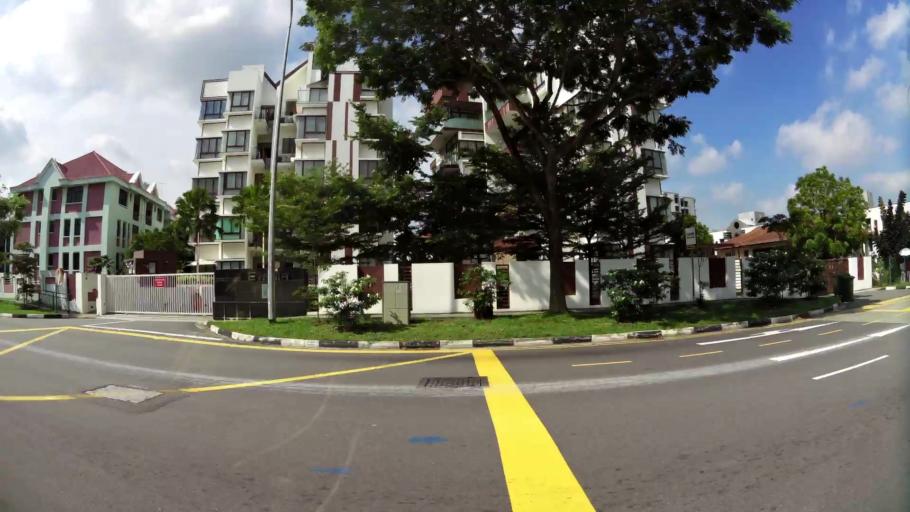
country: SG
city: Singapore
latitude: 1.3505
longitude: 103.8794
